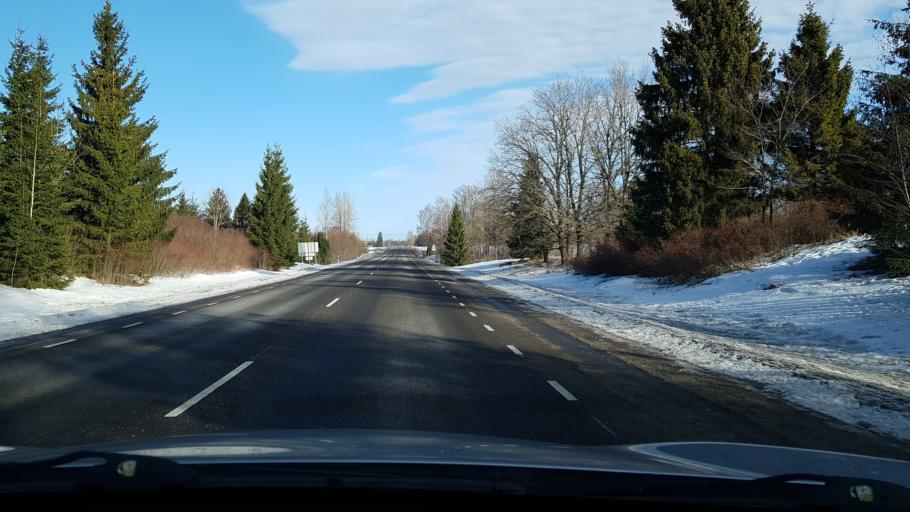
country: EE
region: Viljandimaa
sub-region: Viljandi linn
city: Viljandi
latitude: 58.4101
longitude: 25.5943
